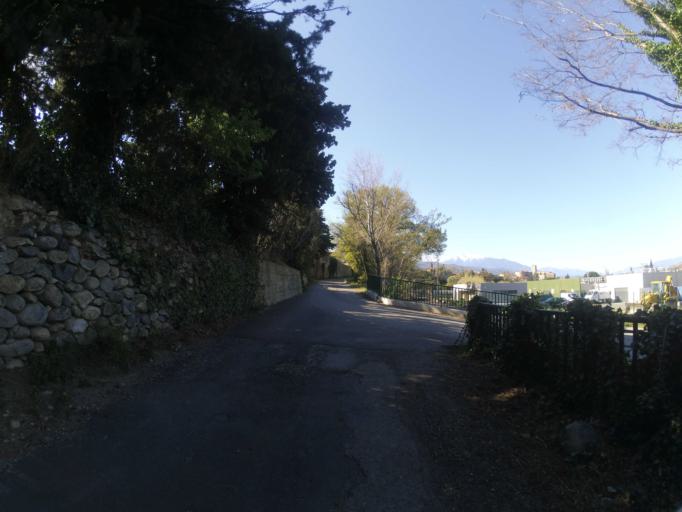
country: FR
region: Languedoc-Roussillon
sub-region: Departement des Pyrenees-Orientales
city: Ille-sur-Tet
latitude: 42.6758
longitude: 2.6257
